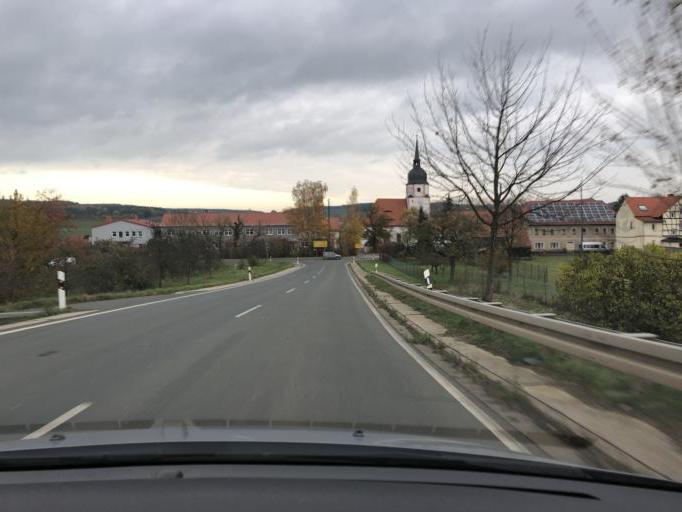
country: DE
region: Thuringia
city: Dreitzsch
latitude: 50.7383
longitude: 11.7993
